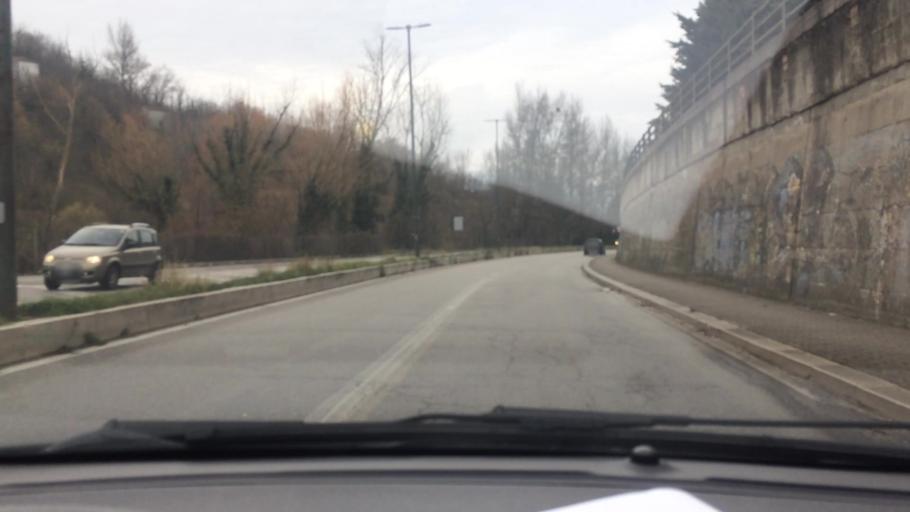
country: IT
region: Basilicate
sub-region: Provincia di Potenza
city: Potenza
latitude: 40.6357
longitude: 15.7953
